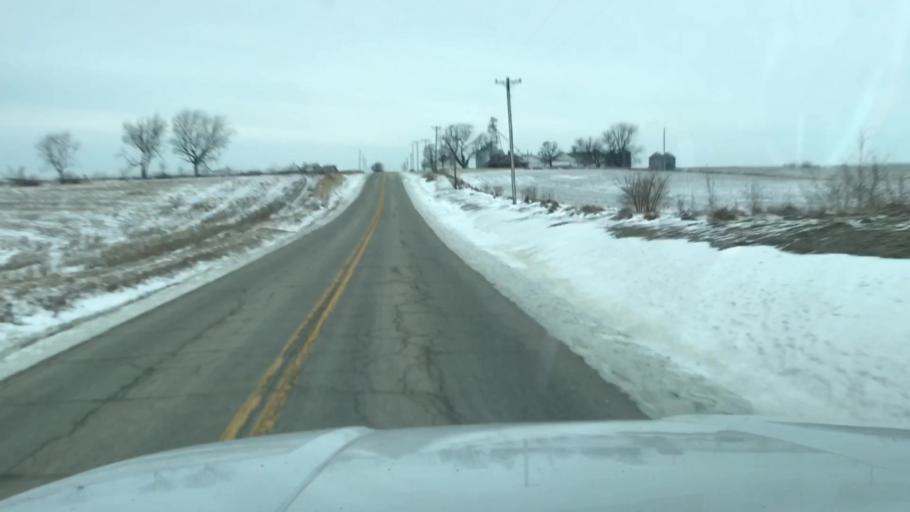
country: US
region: Missouri
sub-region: Andrew County
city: Savannah
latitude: 40.0248
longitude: -94.9343
